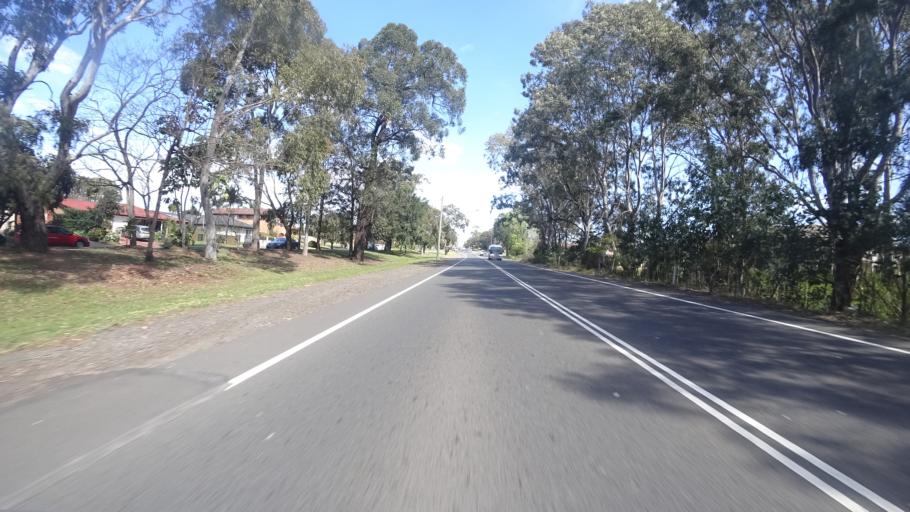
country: AU
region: New South Wales
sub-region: Fairfield
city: Chipping Norton
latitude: -33.9153
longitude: 150.9569
